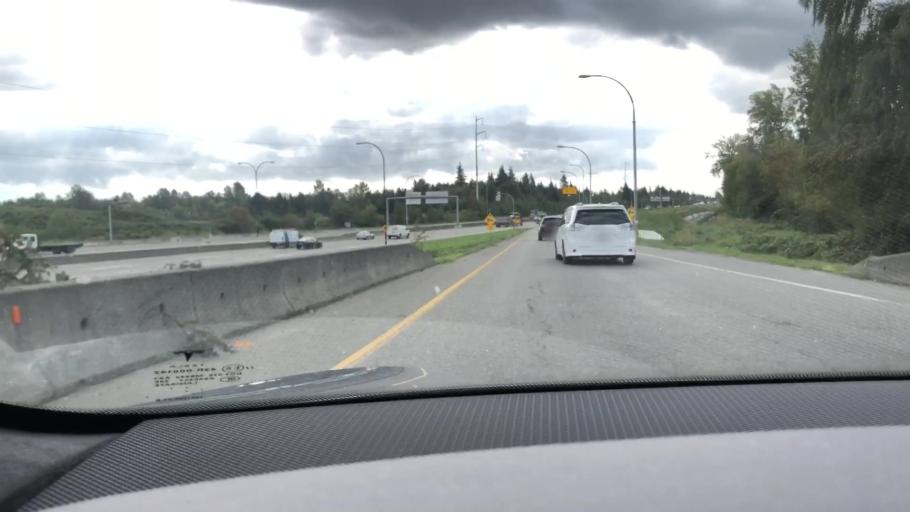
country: CA
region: British Columbia
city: Richmond
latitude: 49.1696
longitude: -123.0880
